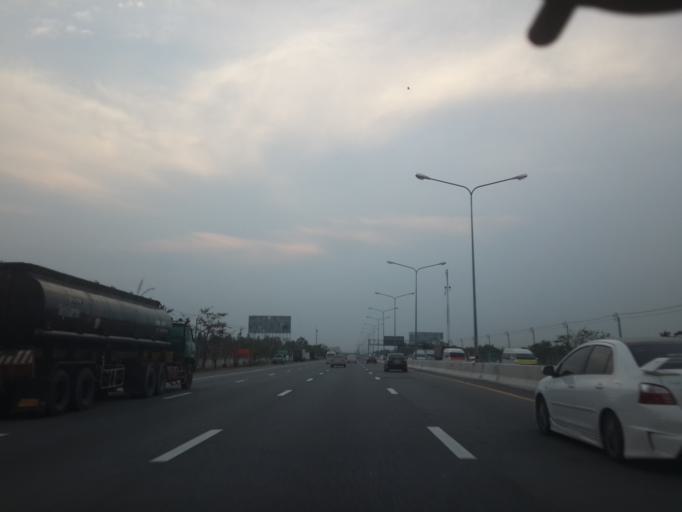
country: TH
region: Bangkok
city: Lat Krabang
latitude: 13.7340
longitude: 100.8009
